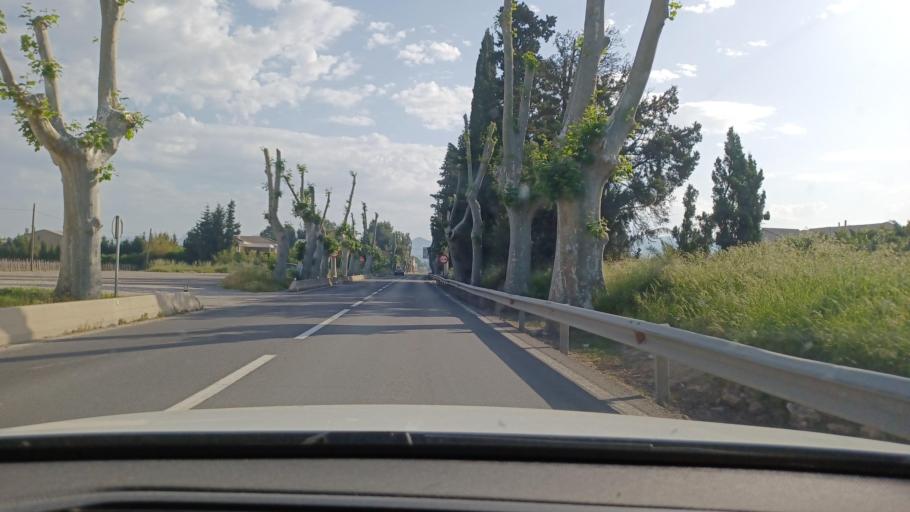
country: ES
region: Catalonia
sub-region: Provincia de Tarragona
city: Tortosa
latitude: 40.8029
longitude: 0.5032
